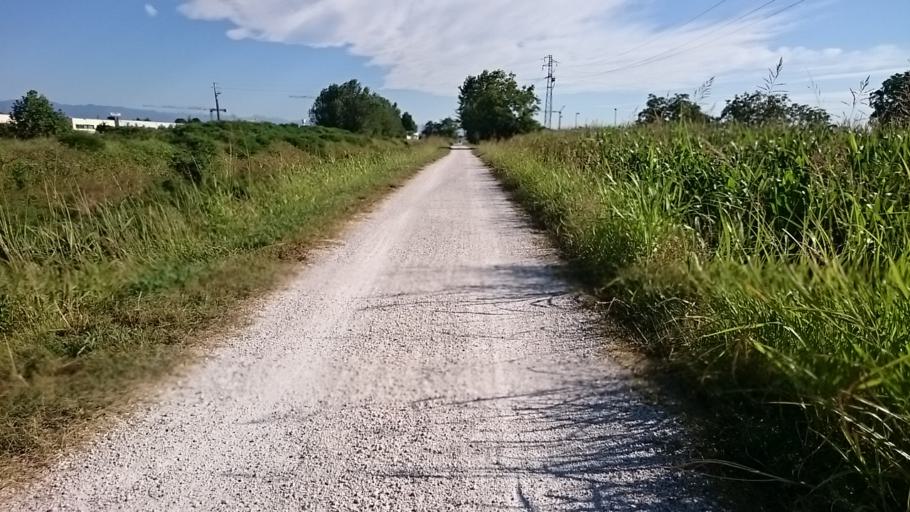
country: IT
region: Veneto
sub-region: Provincia di Padova
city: Borgoricco-San Michele delle Badesse-Sant'Eufemia
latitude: 45.5467
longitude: 11.9298
